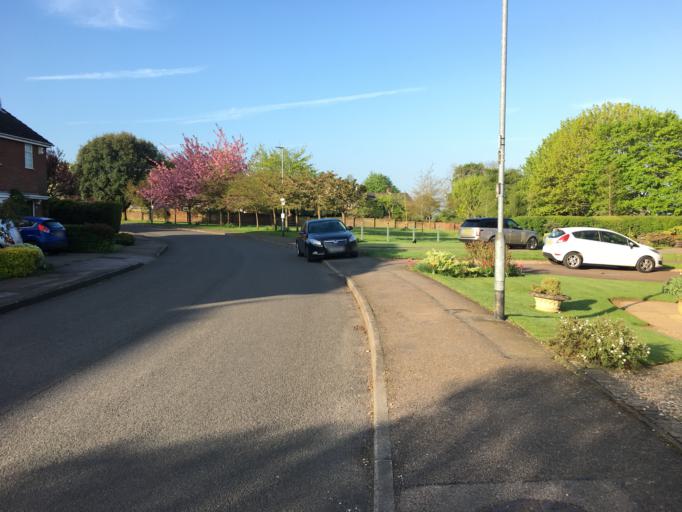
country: GB
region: England
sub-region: Leicestershire
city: Houghton on the Hill
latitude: 52.6254
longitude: -1.0032
